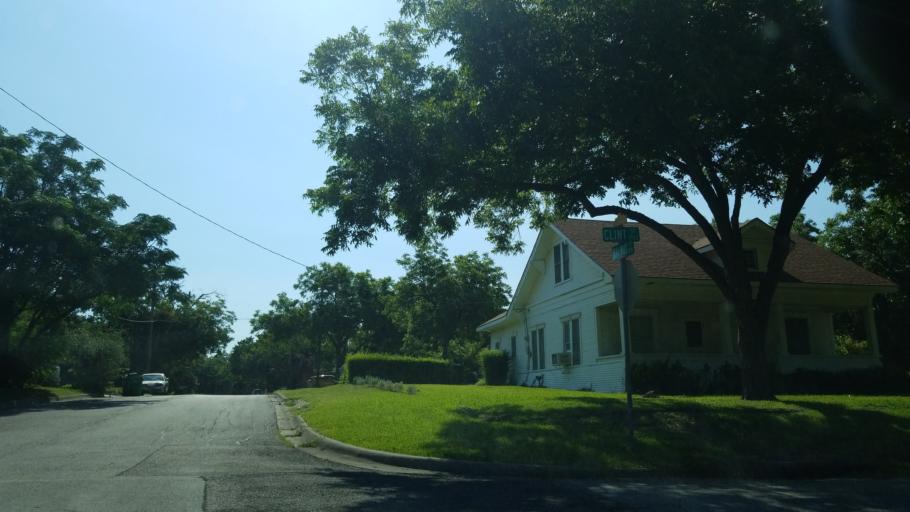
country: US
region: Texas
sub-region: Dallas County
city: Carrollton
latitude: 32.9551
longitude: -96.9015
